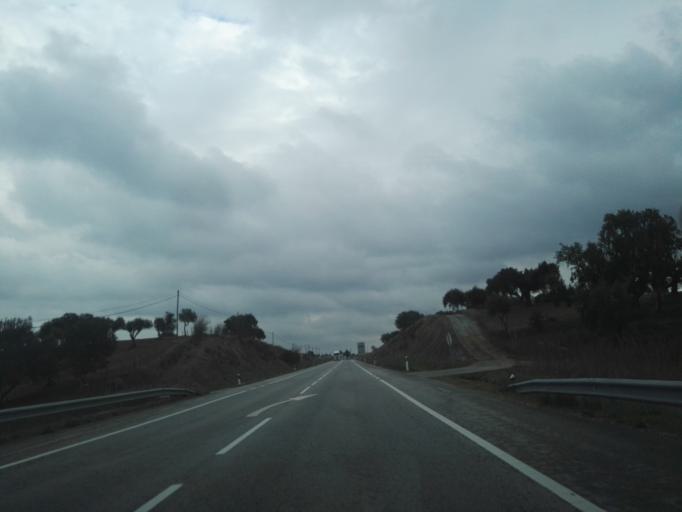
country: PT
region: Portalegre
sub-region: Arronches
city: Arronches
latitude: 39.1375
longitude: -7.2947
